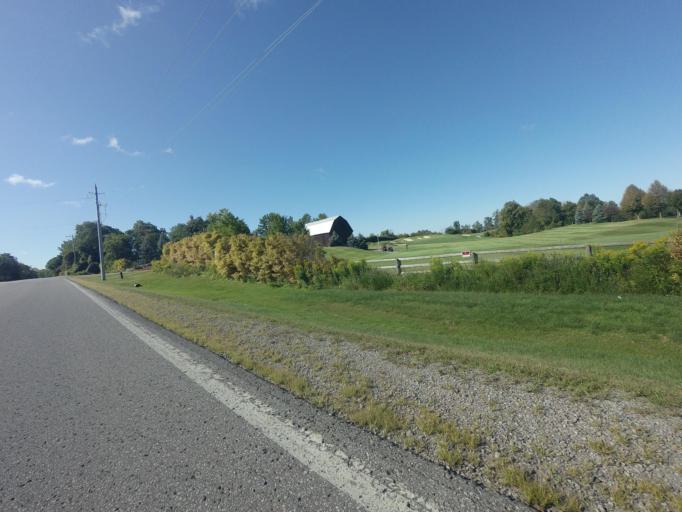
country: CA
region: Ontario
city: Newmarket
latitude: 44.0440
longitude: -79.5566
